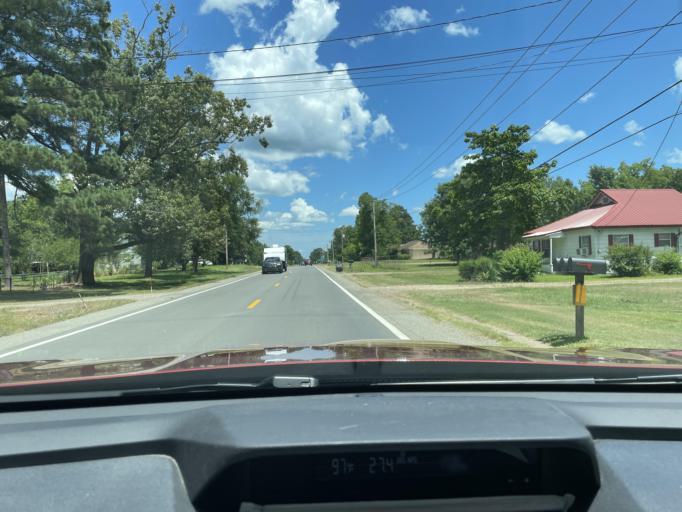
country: US
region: Arkansas
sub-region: Drew County
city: Monticello
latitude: 33.6284
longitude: -91.7636
